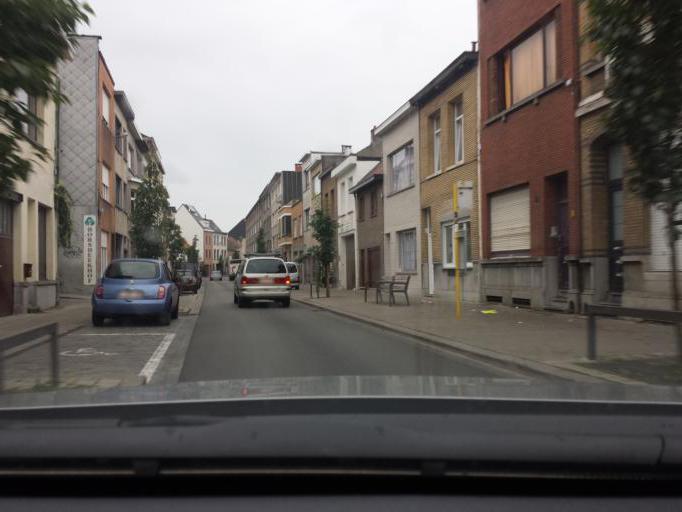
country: BE
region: Flanders
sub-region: Provincie Antwerpen
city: Antwerpen
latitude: 51.2185
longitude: 4.4399
